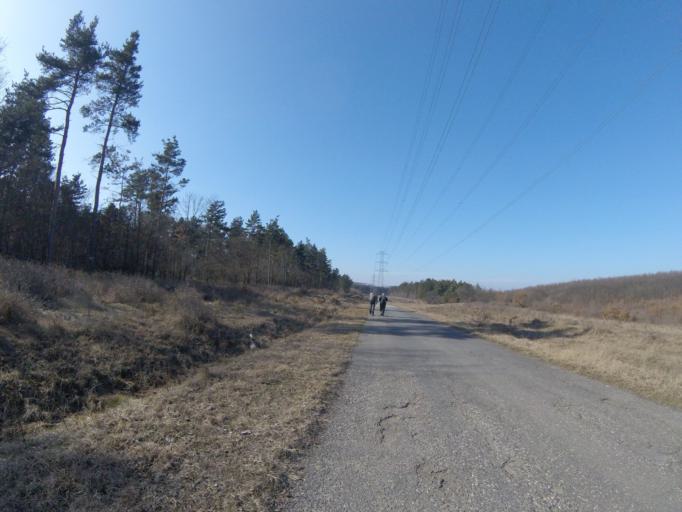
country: HU
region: Komarom-Esztergom
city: Oroszlany
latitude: 47.4555
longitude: 18.3697
